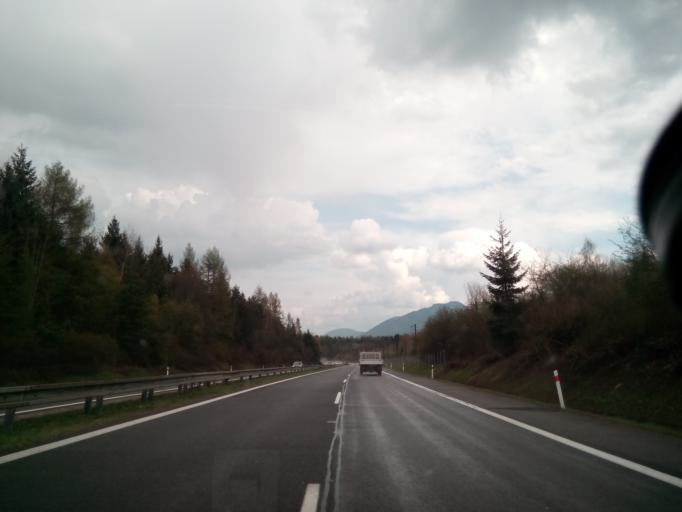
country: SK
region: Zilinsky
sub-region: Okres Liptovsky Mikulas
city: Liptovsky Mikulas
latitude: 49.0900
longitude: 19.5307
